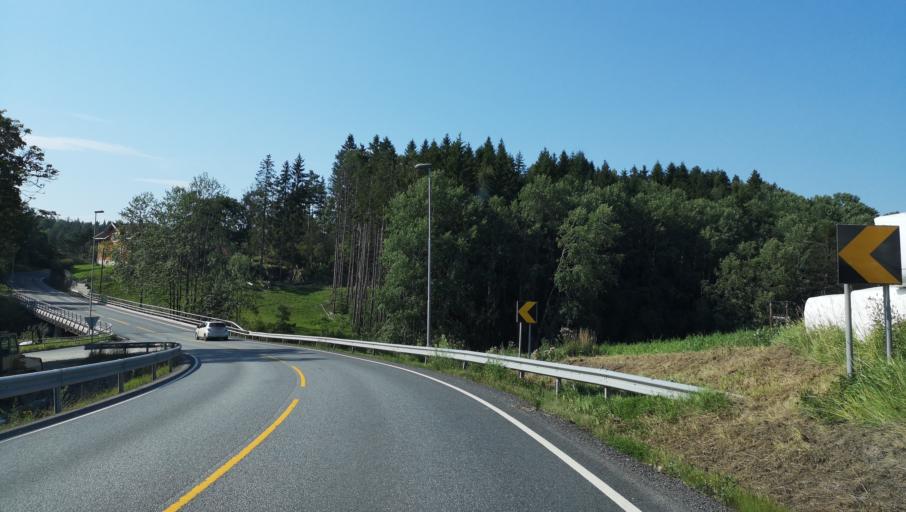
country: NO
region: Ostfold
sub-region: Valer
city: Kirkebygda
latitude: 59.5479
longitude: 10.8471
